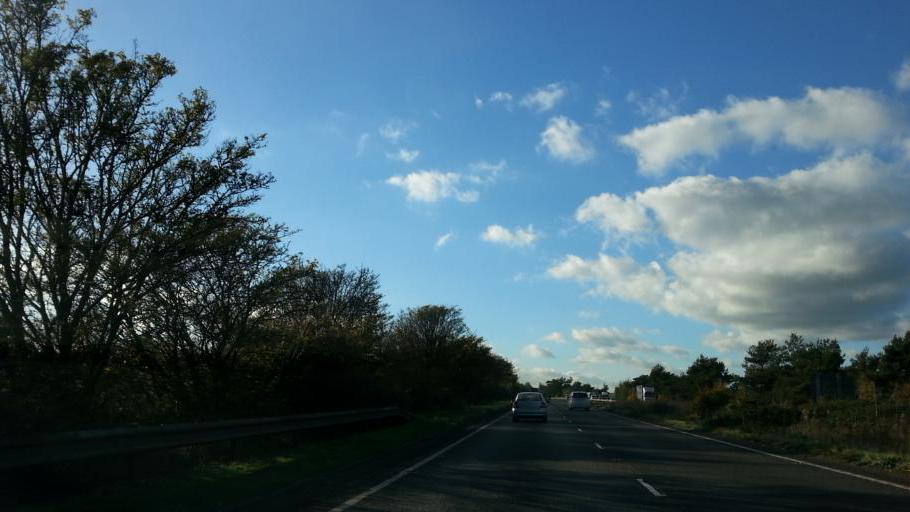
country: GB
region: England
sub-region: Suffolk
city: Bury St Edmunds
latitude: 52.2648
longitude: 0.5925
